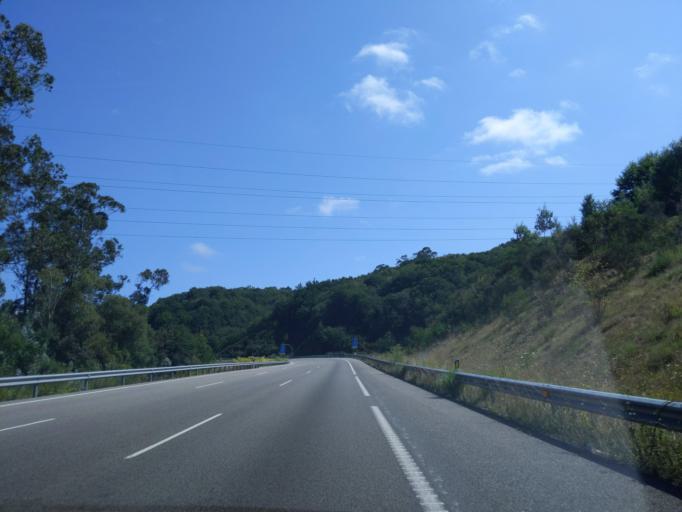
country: ES
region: Asturias
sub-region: Province of Asturias
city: Sama
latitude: 43.3353
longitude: -5.7087
